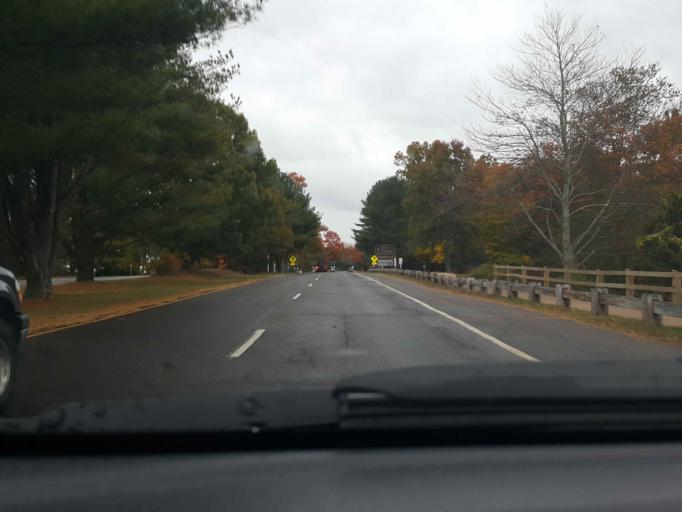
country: US
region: Connecticut
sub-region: Middlesex County
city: Clinton
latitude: 41.2721
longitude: -72.5597
